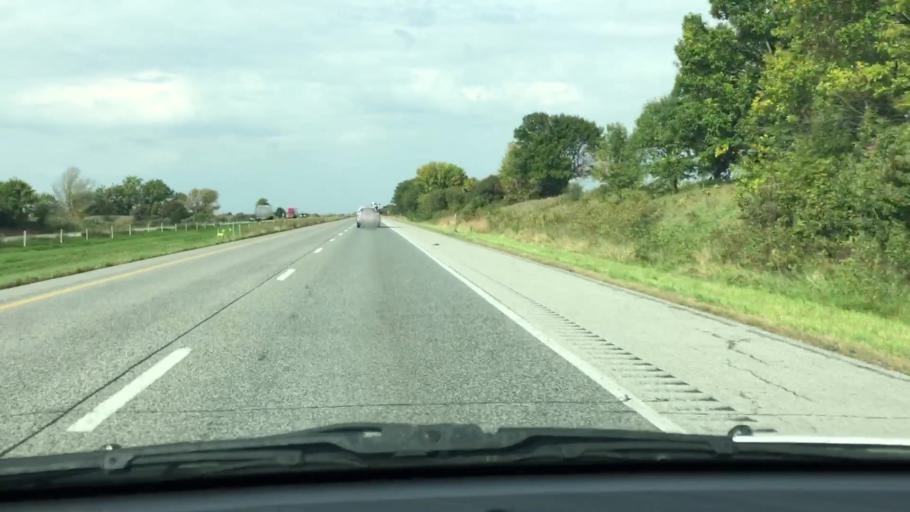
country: US
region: Illinois
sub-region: Rock Island County
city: Hampton
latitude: 41.5972
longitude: -90.4028
